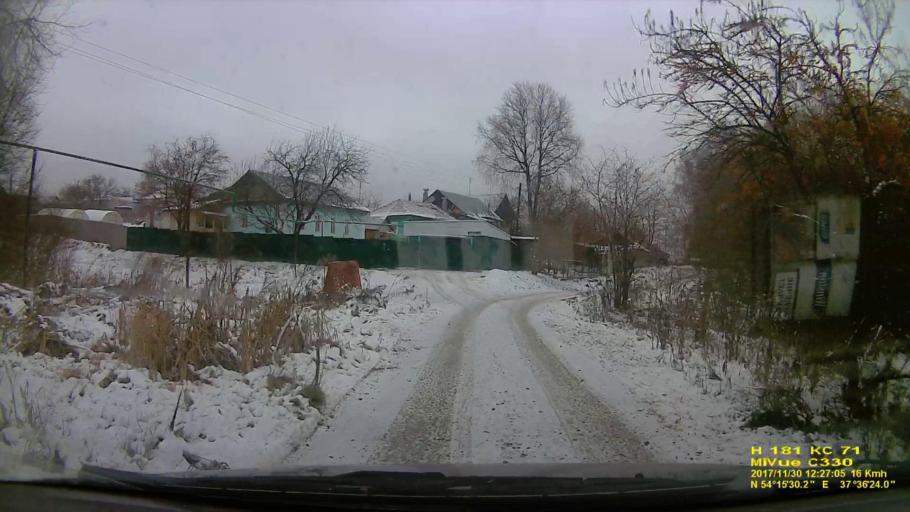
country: RU
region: Tula
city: Gorelki
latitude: 54.2584
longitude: 37.6069
